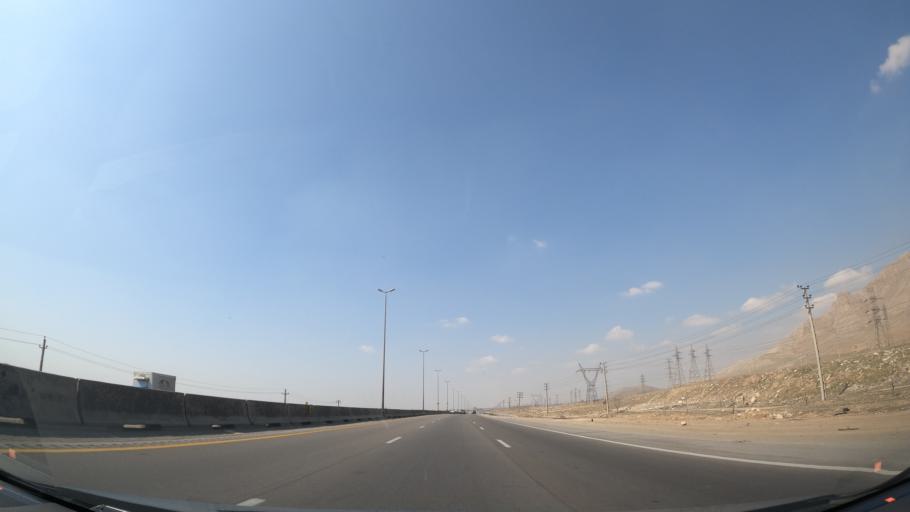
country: IR
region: Qazvin
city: Abyek
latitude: 36.0532
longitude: 50.5128
